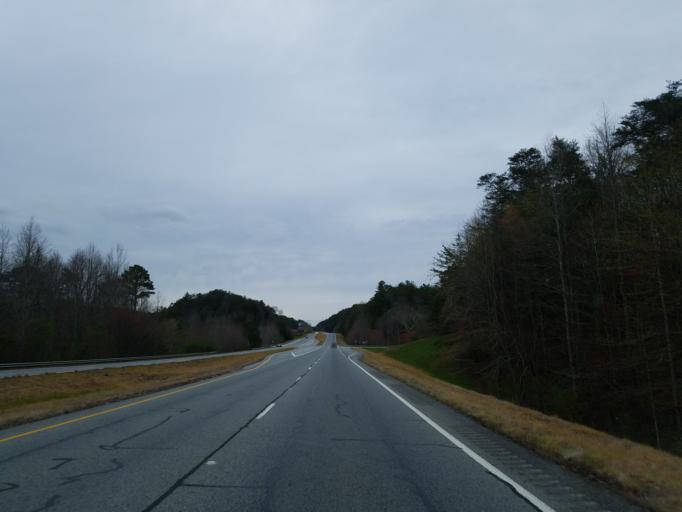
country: US
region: Georgia
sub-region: Fannin County
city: Blue Ridge
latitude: 34.7967
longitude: -84.3800
